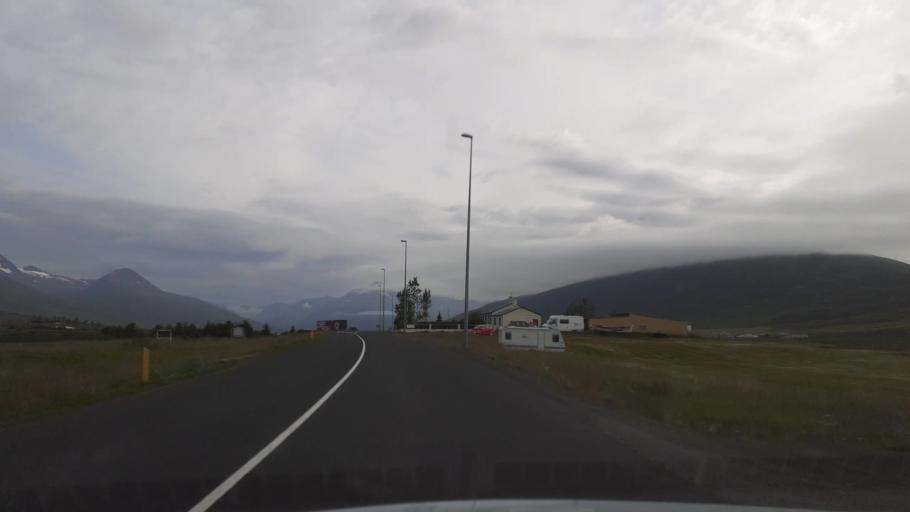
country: IS
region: Northeast
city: Dalvik
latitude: 65.9655
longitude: -18.5327
